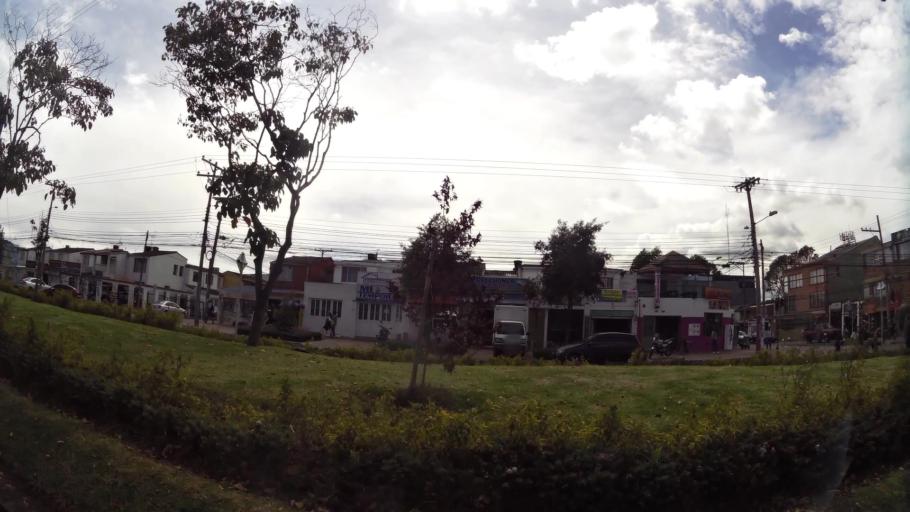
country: CO
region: Bogota D.C.
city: Bogota
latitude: 4.6255
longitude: -74.1366
